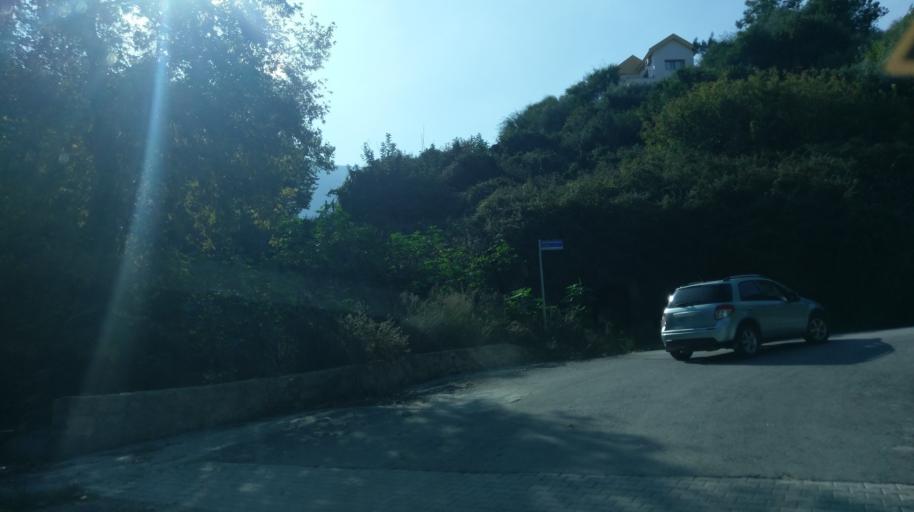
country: CY
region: Keryneia
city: Kyrenia
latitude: 35.3284
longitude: 33.2583
